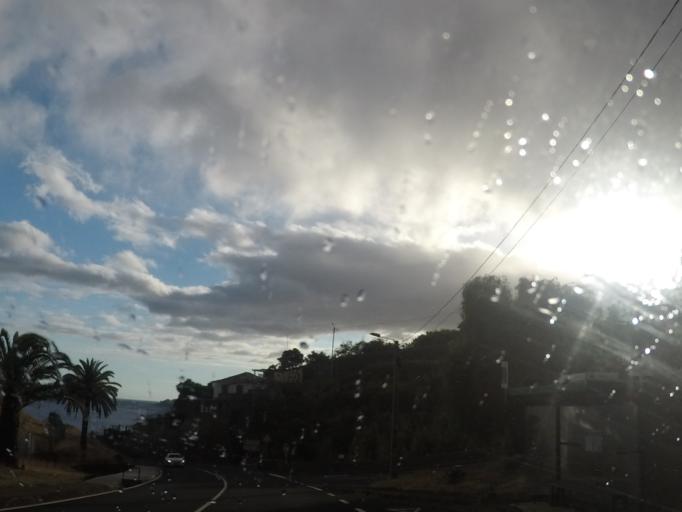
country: PT
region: Madeira
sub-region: Santa Cruz
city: Santa Cruz
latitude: 32.6905
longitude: -16.7852
